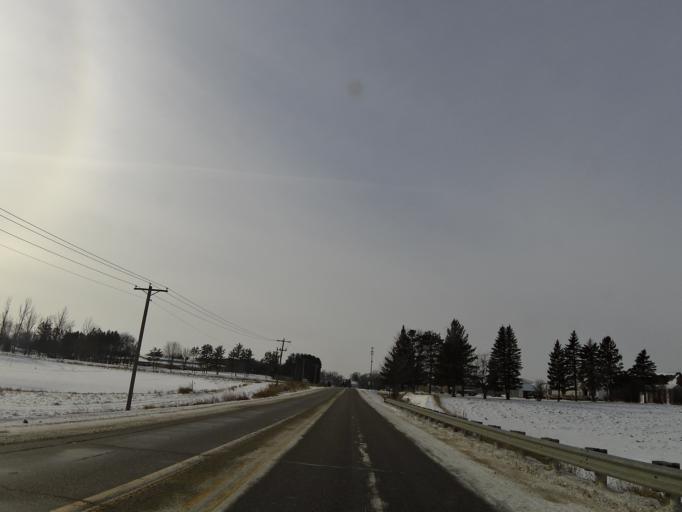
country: US
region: Minnesota
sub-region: Carver County
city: Mayer
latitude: 44.8931
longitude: -93.8827
